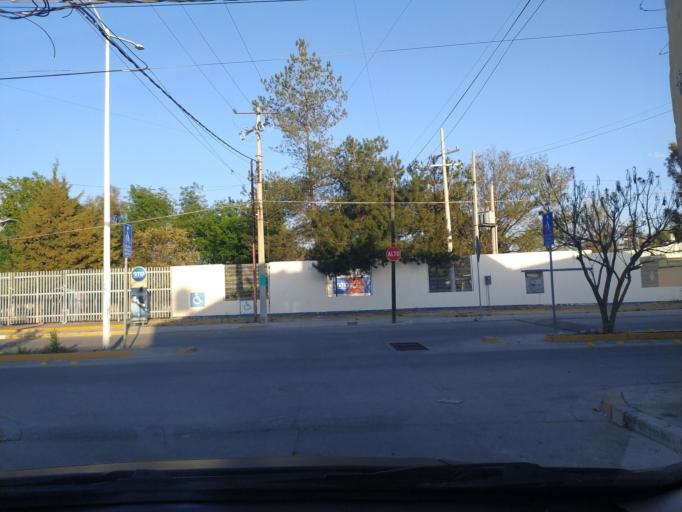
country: MX
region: Guanajuato
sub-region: San Francisco del Rincon
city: Fraccionamiento la Mezquitera
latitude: 21.0113
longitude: -101.8410
